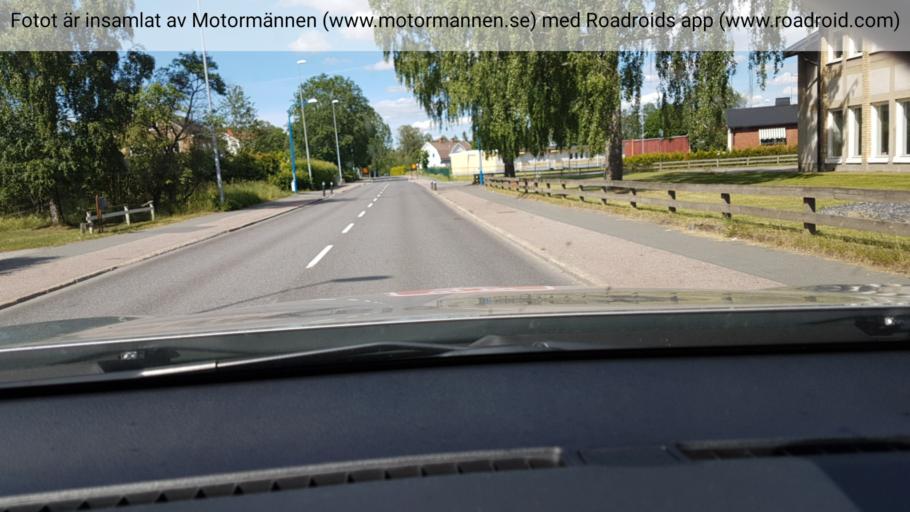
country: SE
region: Joenkoeping
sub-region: Vaggeryds Kommun
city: Vaggeryd
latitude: 57.5012
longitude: 14.1415
